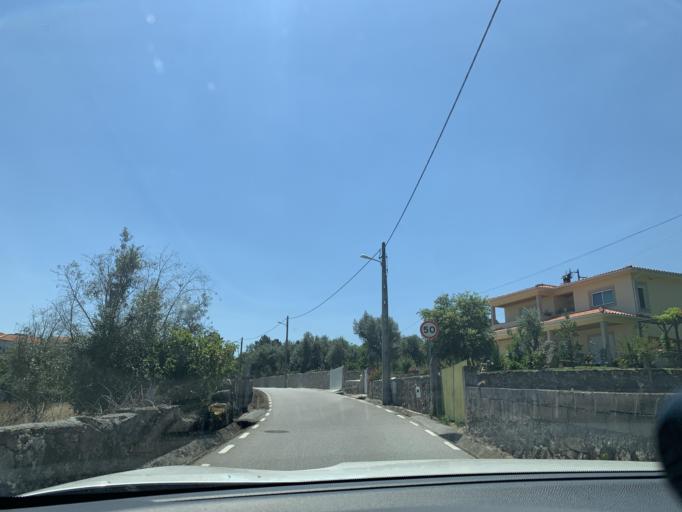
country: PT
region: Viseu
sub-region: Mangualde
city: Mangualde
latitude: 40.5599
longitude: -7.7224
